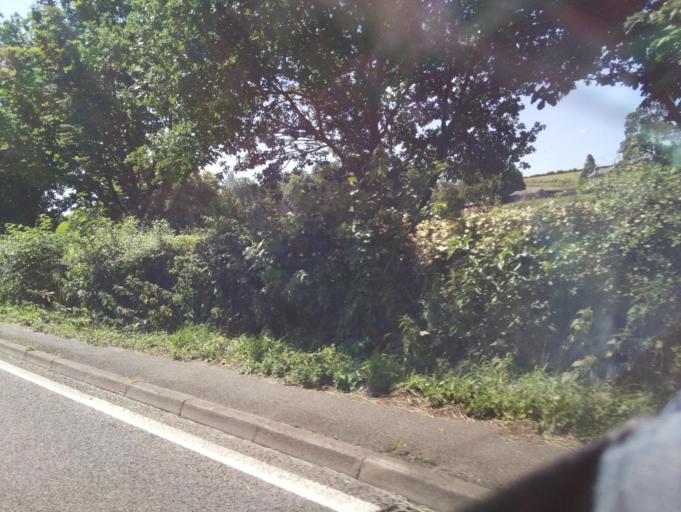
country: GB
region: England
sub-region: Derbyshire
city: Bakewell
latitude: 53.2045
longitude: -1.6656
